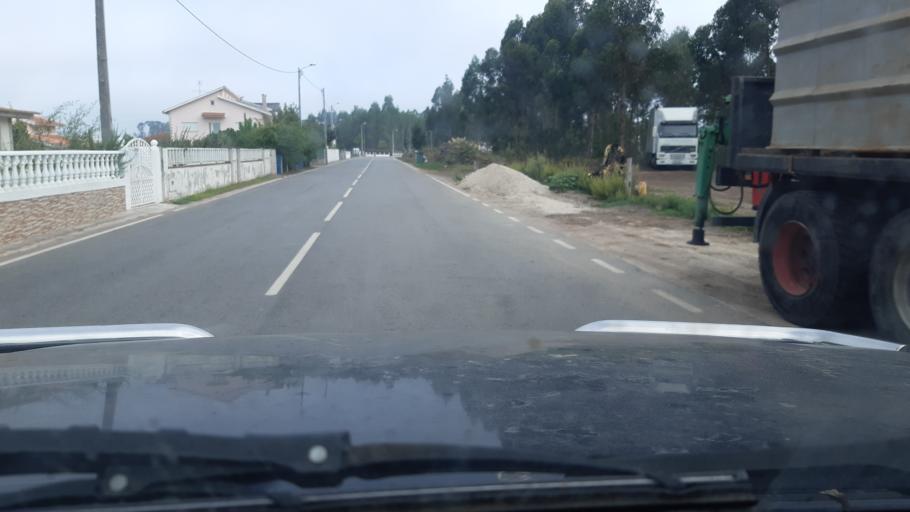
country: PT
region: Aveiro
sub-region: Agueda
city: Agueda
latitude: 40.5834
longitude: -8.4568
